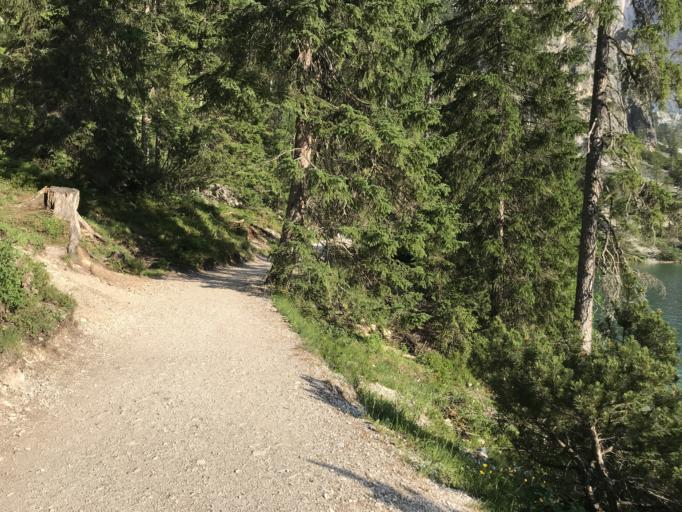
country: IT
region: Trentino-Alto Adige
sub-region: Bolzano
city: Braies
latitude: 46.6921
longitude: 12.0868
